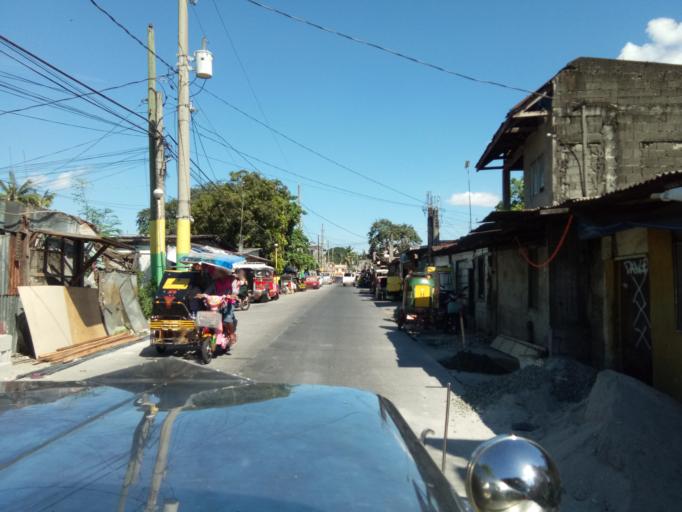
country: PH
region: Calabarzon
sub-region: Province of Cavite
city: Dasmarinas
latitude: 14.3385
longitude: 120.9539
